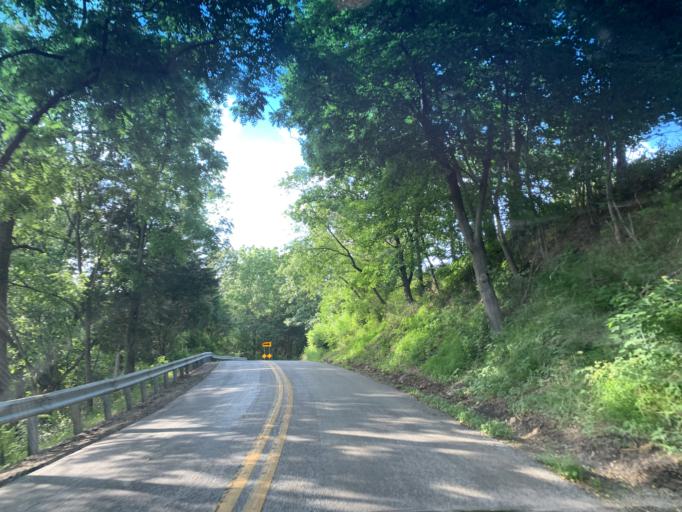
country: US
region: Pennsylvania
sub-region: York County
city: Stewartstown
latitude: 39.7506
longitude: -76.5405
